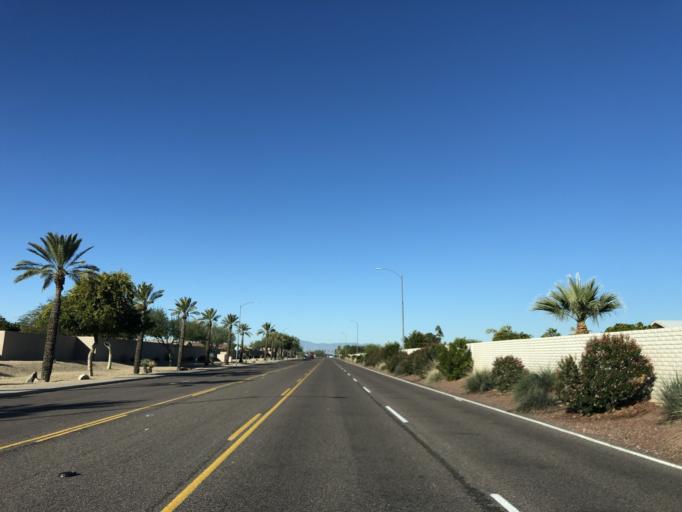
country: US
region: Arizona
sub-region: Maricopa County
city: Sun City West
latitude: 33.6621
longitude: -112.2899
